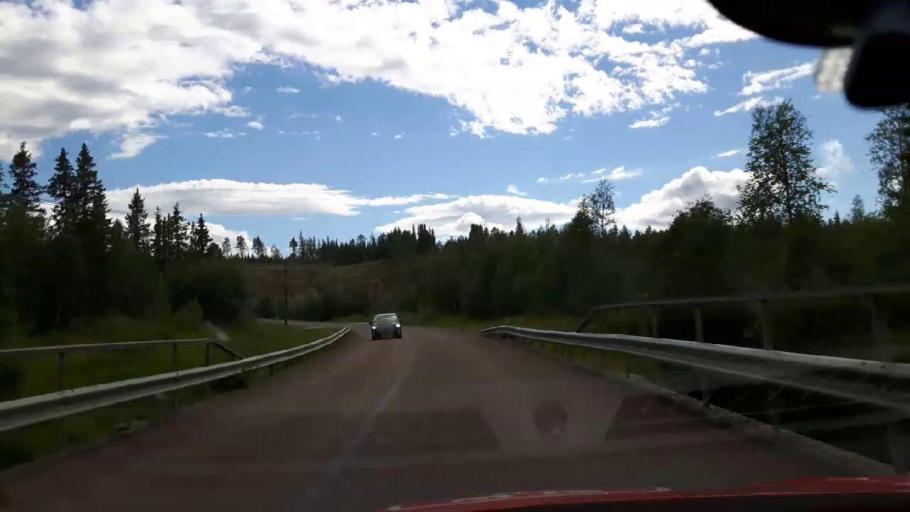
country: SE
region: Jaemtland
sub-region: Are Kommun
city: Are
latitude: 63.3034
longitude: 13.2215
